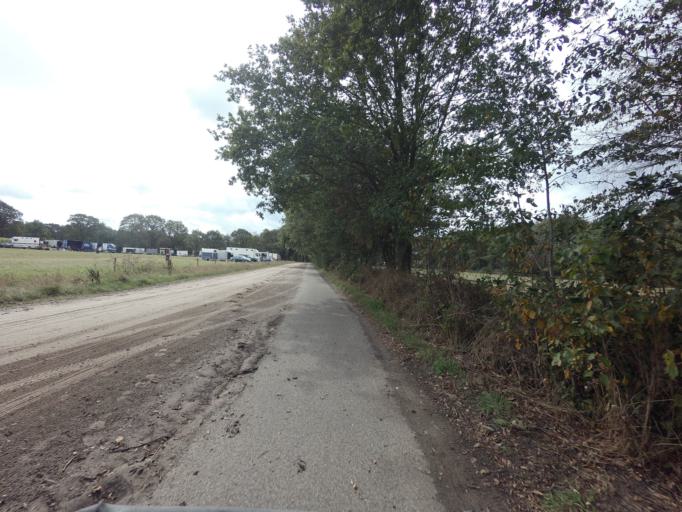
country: NL
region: Drenthe
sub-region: Gemeente Tynaarlo
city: Vries
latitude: 53.0704
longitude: 6.4640
